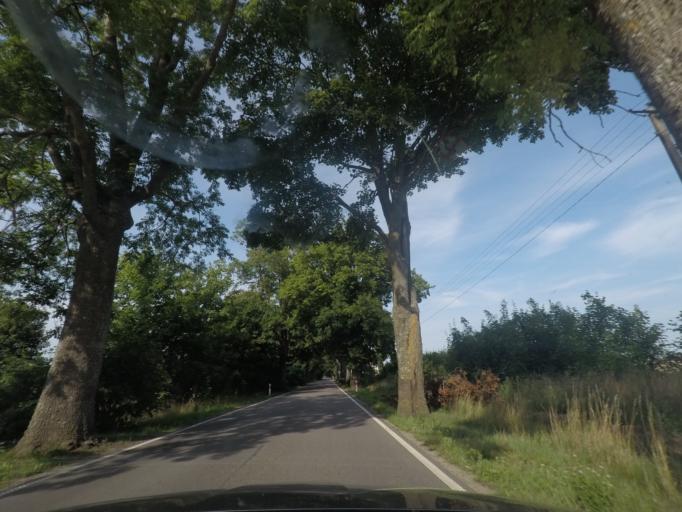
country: PL
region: Pomeranian Voivodeship
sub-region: Powiat leborski
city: Leba
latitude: 54.6405
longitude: 17.5348
